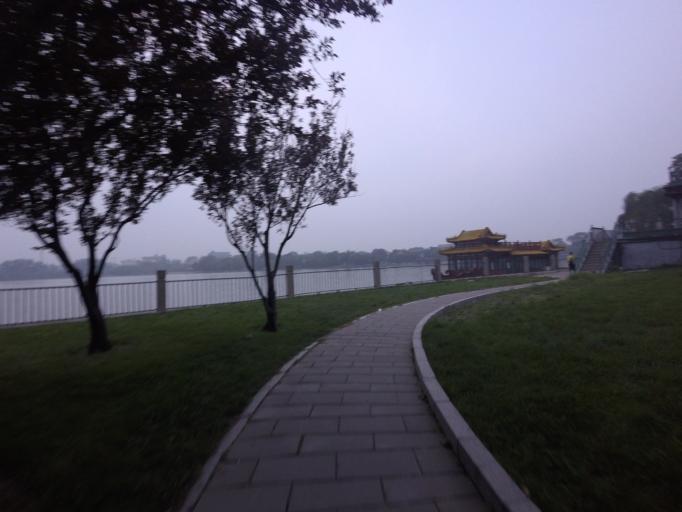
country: CN
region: Beijing
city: Jingshan
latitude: 39.9284
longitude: 116.3852
